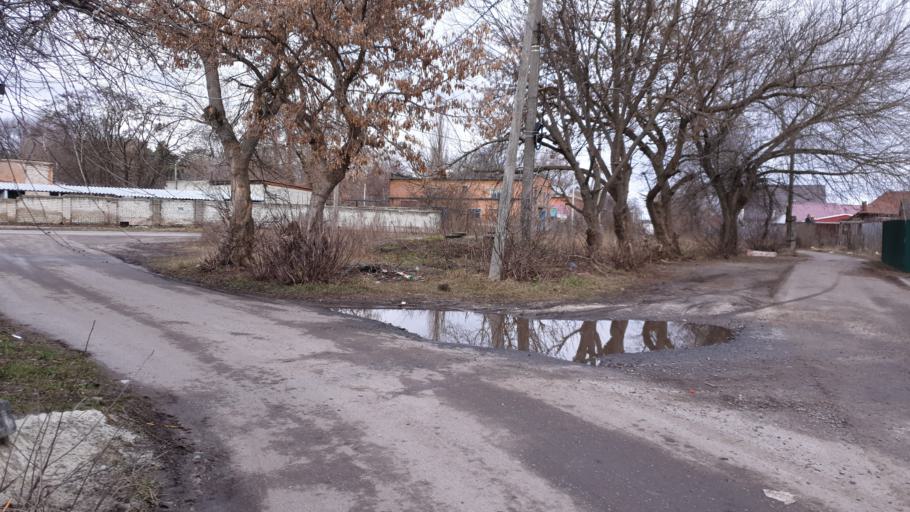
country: RU
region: Kursk
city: Voroshnevo
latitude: 51.6702
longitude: 36.0955
